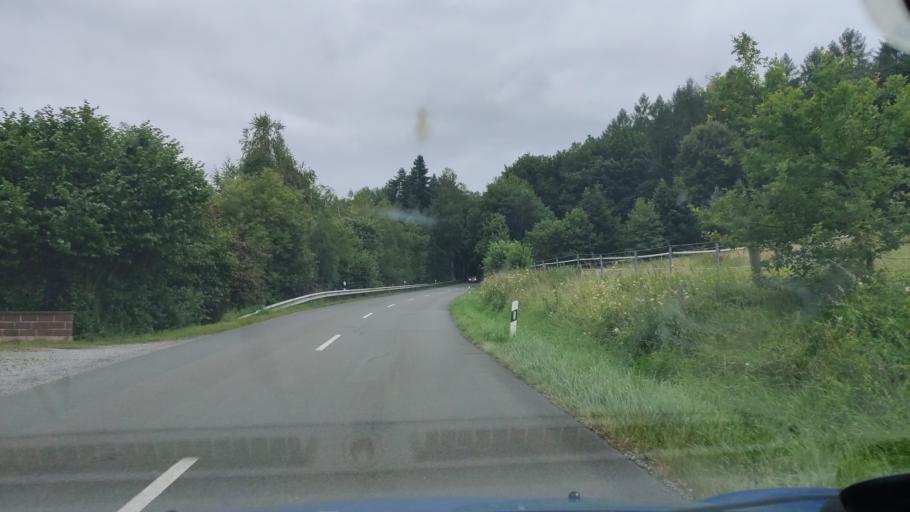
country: DE
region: Lower Saxony
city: Holzminden
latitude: 51.8068
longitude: 9.4786
